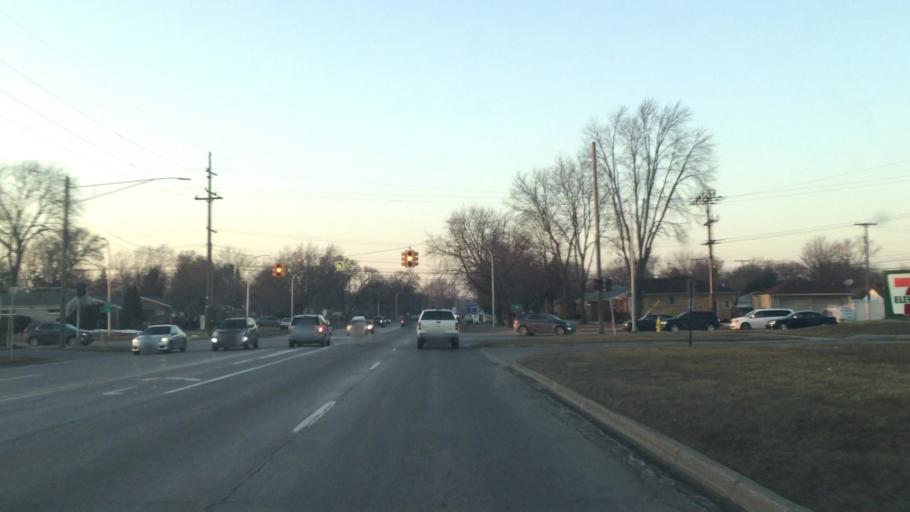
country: US
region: Michigan
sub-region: Wayne County
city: Livonia
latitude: 42.3538
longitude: -83.3516
